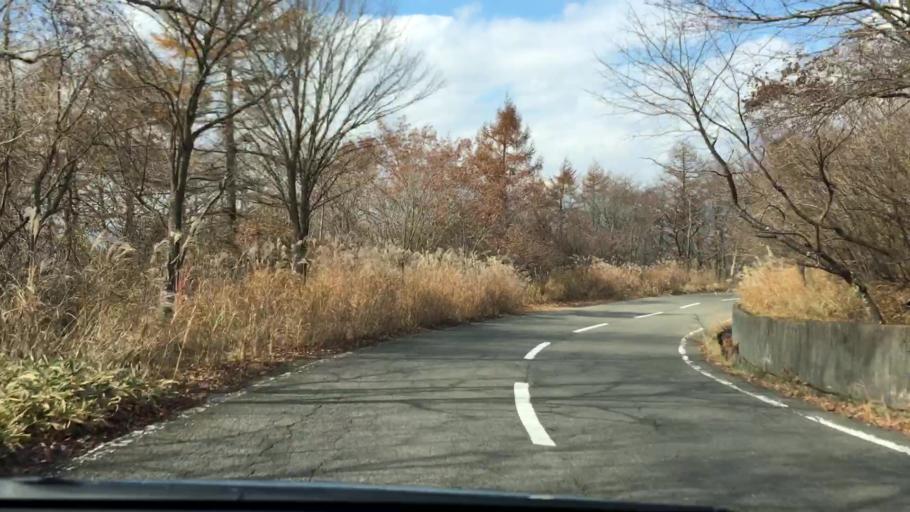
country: JP
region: Shizuoka
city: Gotemba
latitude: 35.4066
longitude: 138.9138
